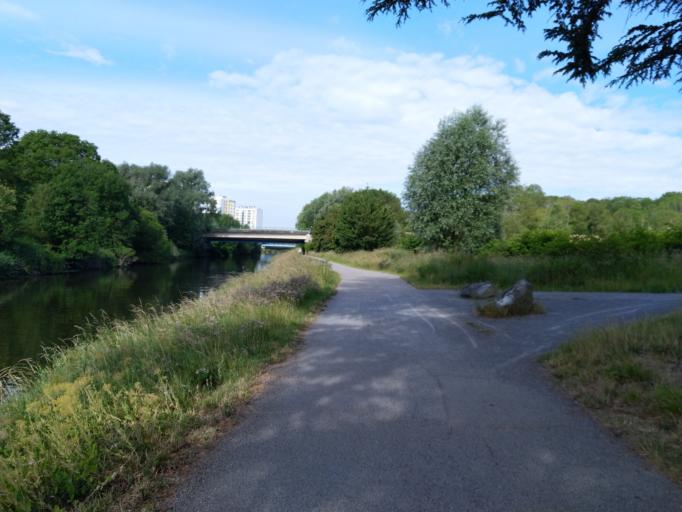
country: FR
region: Nord-Pas-de-Calais
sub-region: Departement du Nord
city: Maubeuge
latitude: 50.2754
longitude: 3.9848
